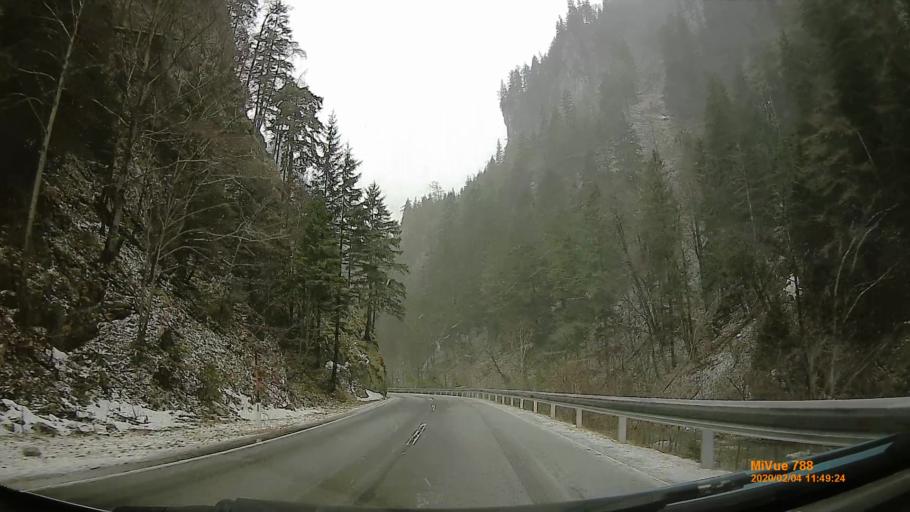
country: AT
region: Styria
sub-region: Politischer Bezirk Bruck-Muerzzuschlag
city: Muerzsteg
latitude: 47.7239
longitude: 15.4843
